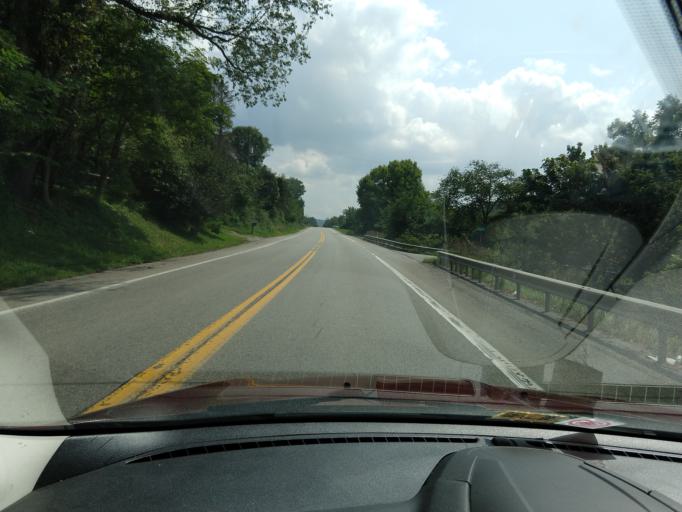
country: US
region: Pennsylvania
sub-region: Washington County
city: McGovern
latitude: 40.1715
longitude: -80.1355
